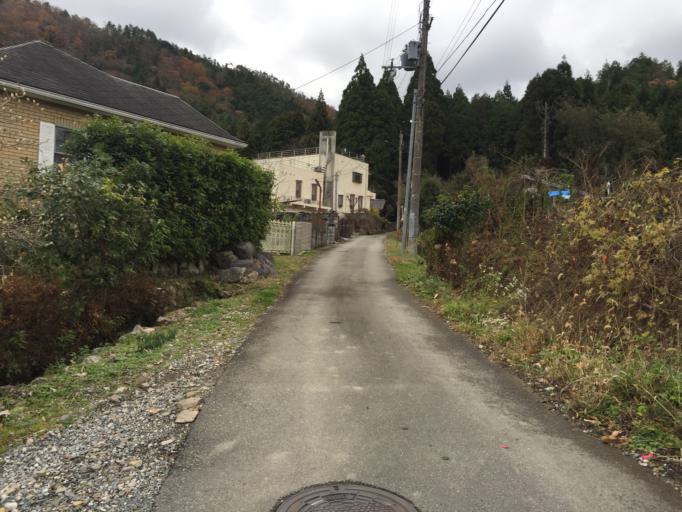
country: JP
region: Kyoto
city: Kameoka
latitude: 34.9860
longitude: 135.5506
